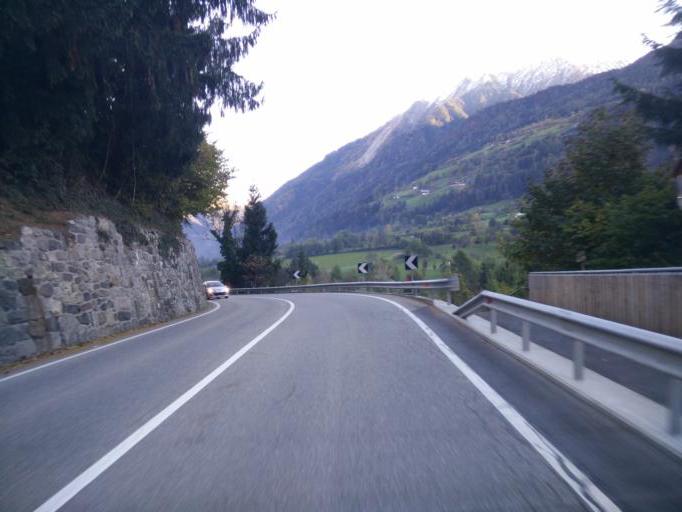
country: IT
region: Trentino-Alto Adige
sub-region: Bolzano
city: San Martino in Passiria
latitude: 46.7687
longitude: 11.2163
